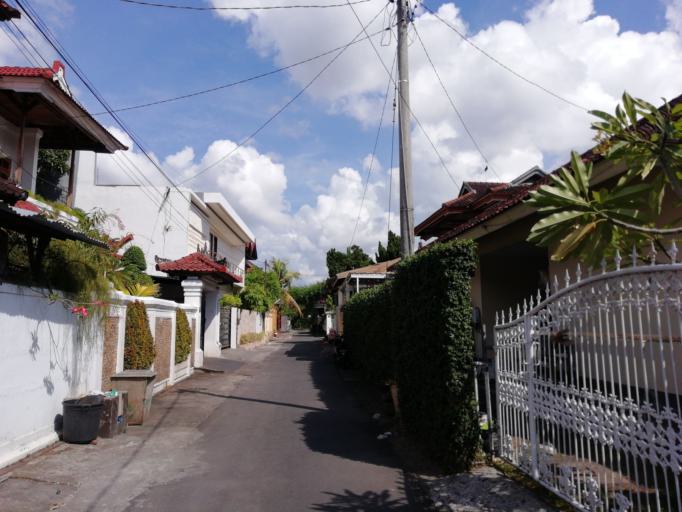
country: ID
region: Bali
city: Denpasar
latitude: -8.6724
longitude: 115.2117
